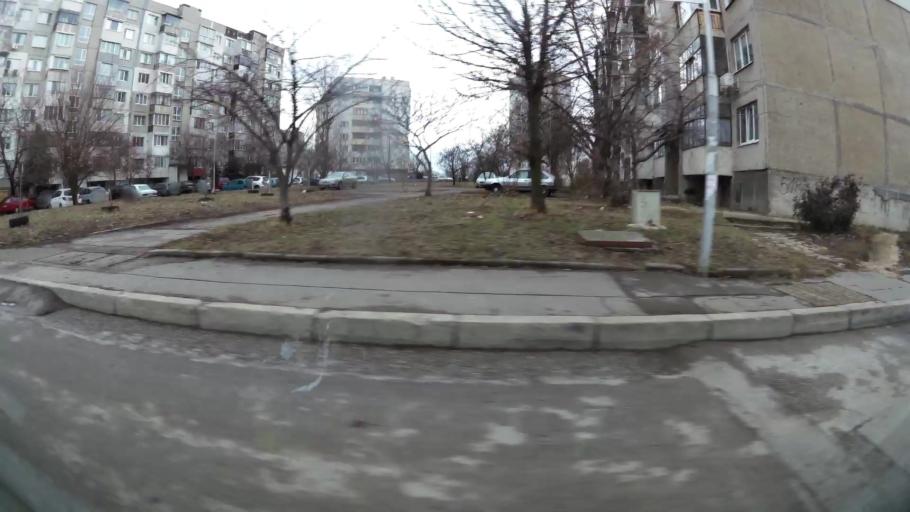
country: BG
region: Sofia-Capital
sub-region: Stolichna Obshtina
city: Sofia
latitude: 42.7376
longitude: 23.2871
